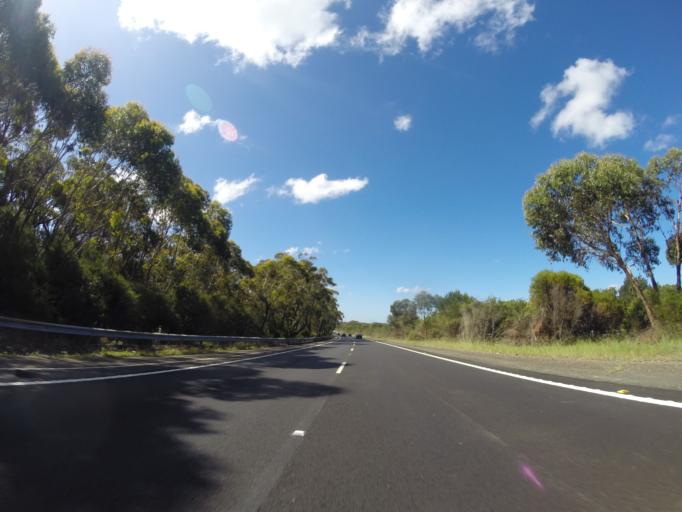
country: AU
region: New South Wales
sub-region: Wollongong
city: Helensburgh
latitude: -34.2372
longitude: 150.9461
